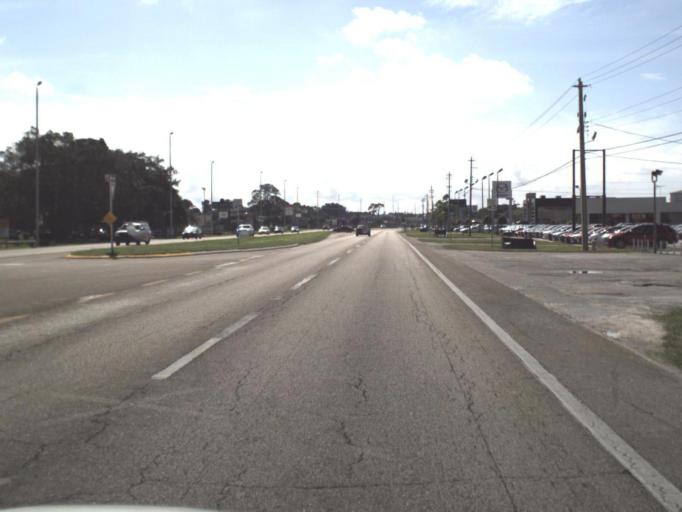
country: US
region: Florida
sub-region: Sarasota County
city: Gulf Gate Estates
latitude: 27.2547
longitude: -82.5174
